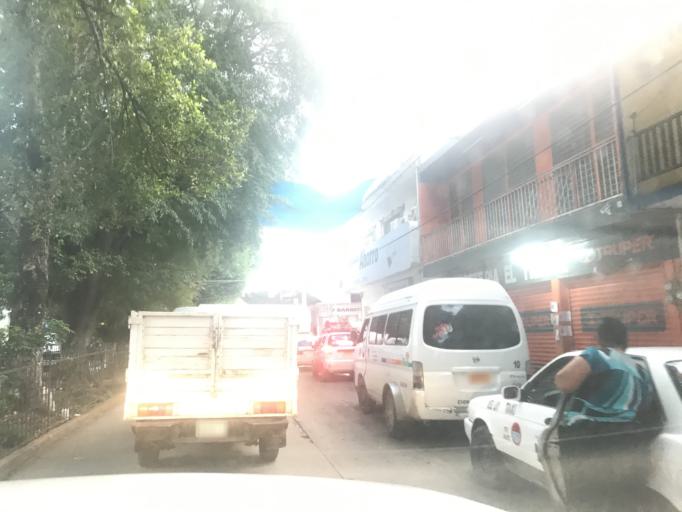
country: MX
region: Morelos
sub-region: Jojutla
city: Jojutla
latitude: 18.6143
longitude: -99.1769
